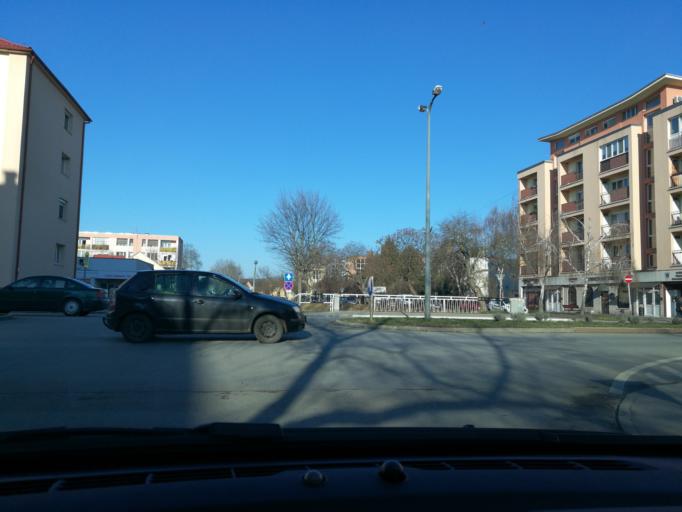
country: HU
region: Szabolcs-Szatmar-Bereg
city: Nyiregyhaza
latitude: 47.9471
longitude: 21.7104
